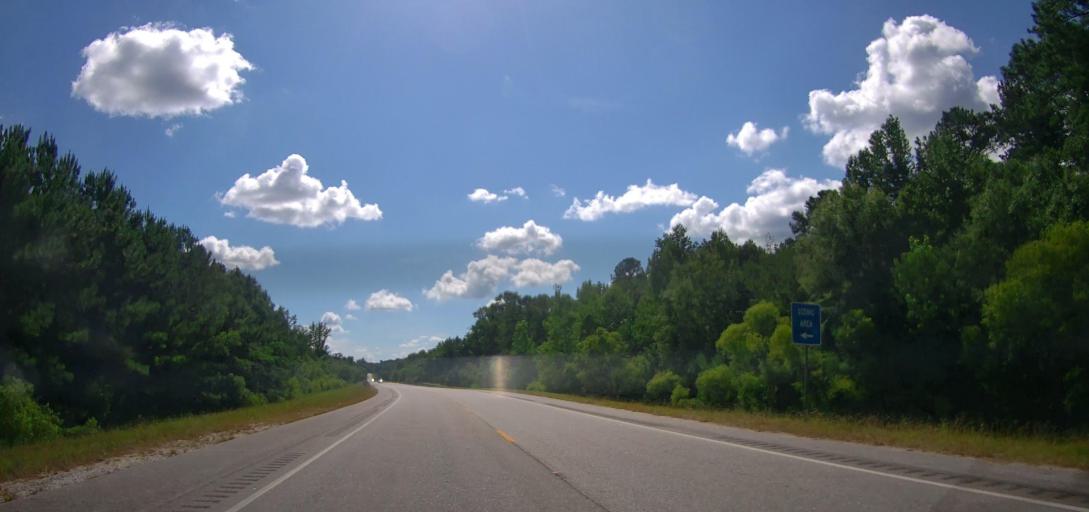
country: US
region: Alabama
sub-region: Macon County
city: Tuskegee
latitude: 32.4435
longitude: -85.6522
